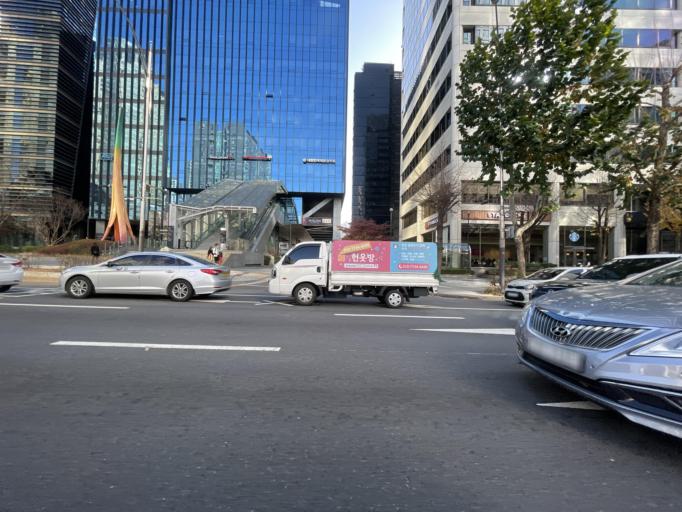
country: KR
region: Seoul
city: Seoul
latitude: 37.5431
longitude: 126.9505
